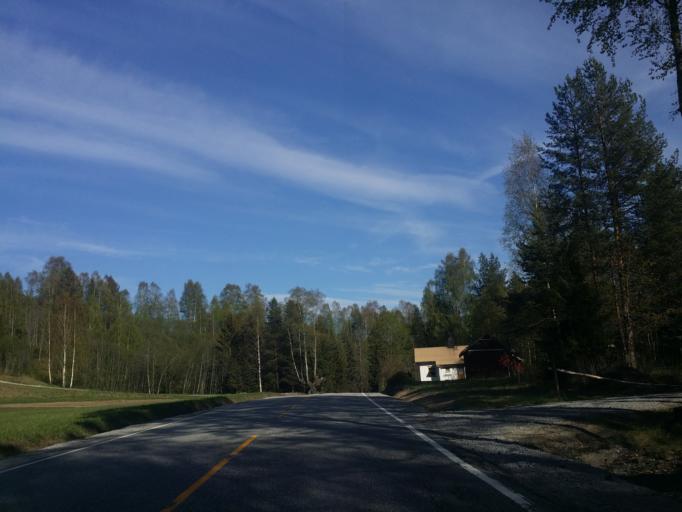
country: NO
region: Telemark
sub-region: Hjartdal
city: Sauland
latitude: 59.6233
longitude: 8.9065
